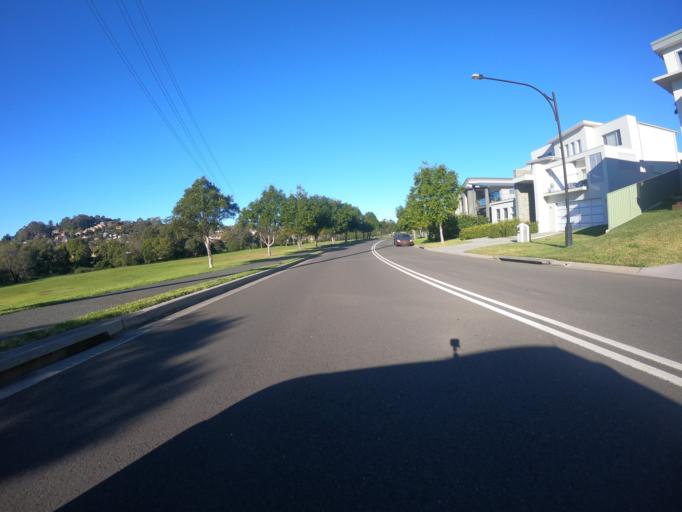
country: AU
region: New South Wales
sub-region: Wollongong
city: Cordeaux Heights
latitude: -34.4376
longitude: 150.8484
